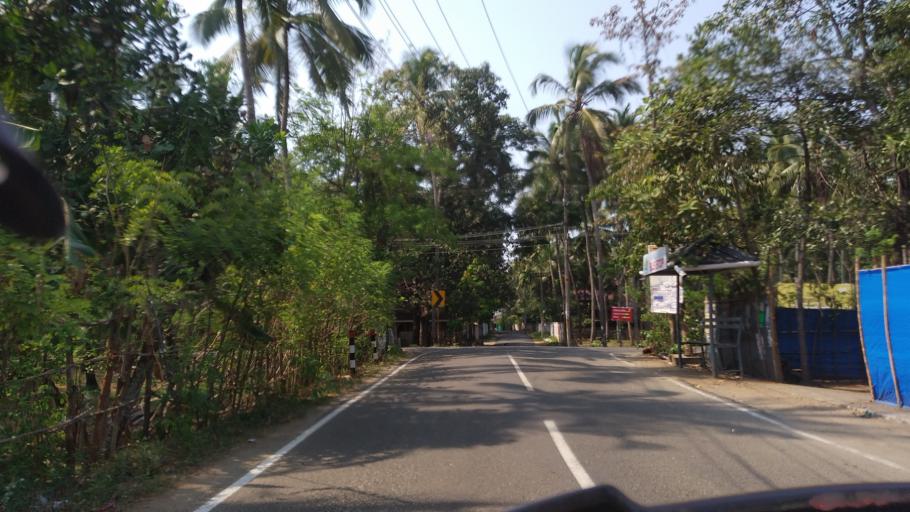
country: IN
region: Kerala
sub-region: Thrissur District
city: Thanniyam
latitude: 10.3982
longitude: 76.0942
